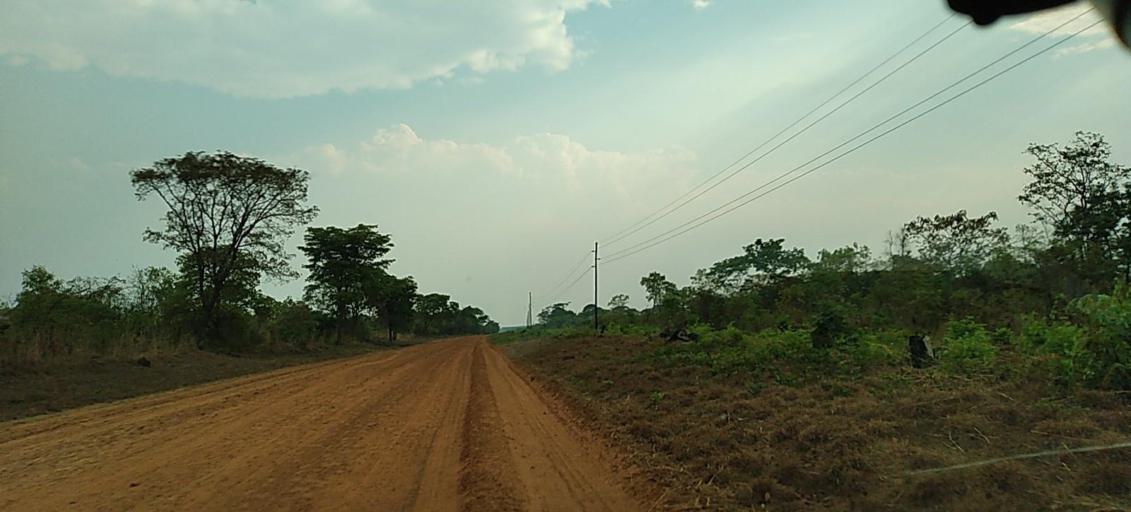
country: ZM
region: North-Western
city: Kabompo
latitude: -13.8998
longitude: 23.6561
